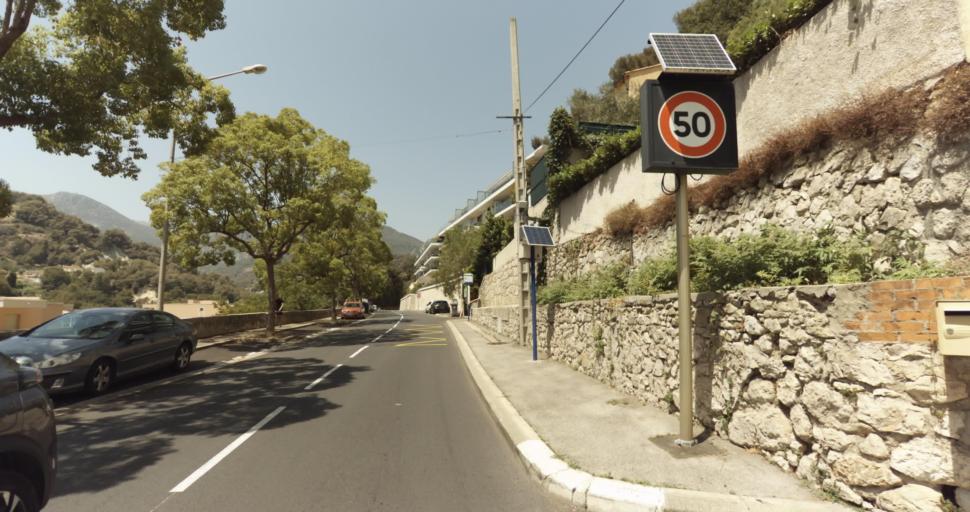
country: FR
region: Provence-Alpes-Cote d'Azur
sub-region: Departement des Alpes-Maritimes
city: Roquebrune-Cap-Martin
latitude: 43.7707
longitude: 7.4794
